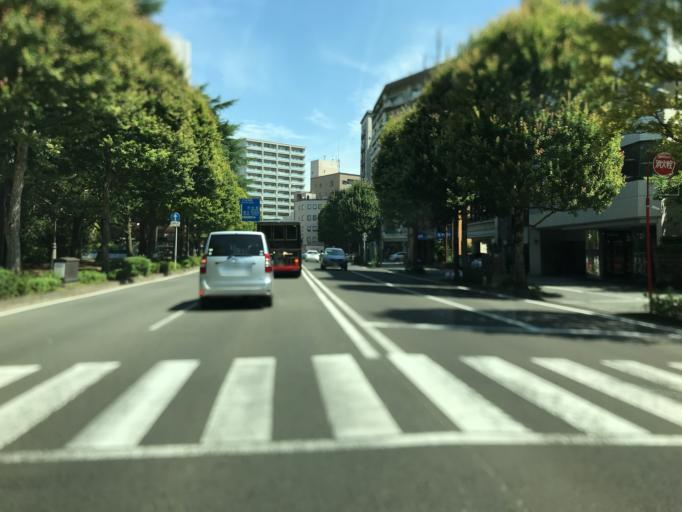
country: JP
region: Miyagi
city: Sendai
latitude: 38.2634
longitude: 140.8630
